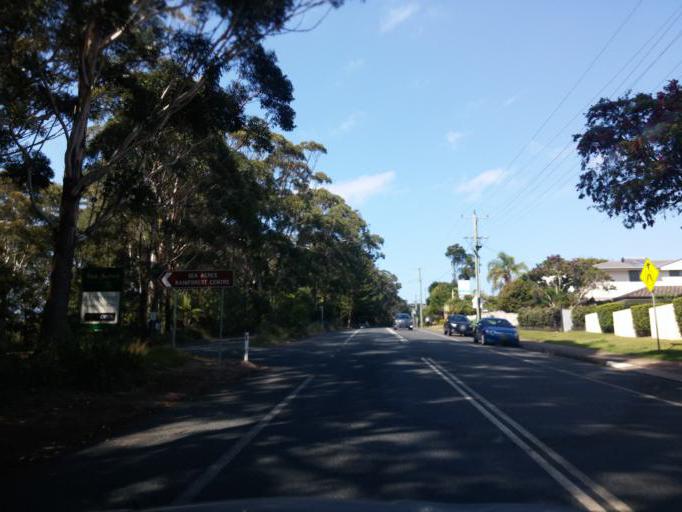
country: AU
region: New South Wales
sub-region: Port Macquarie-Hastings
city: Port Macquarie
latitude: -31.4604
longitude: 152.9294
